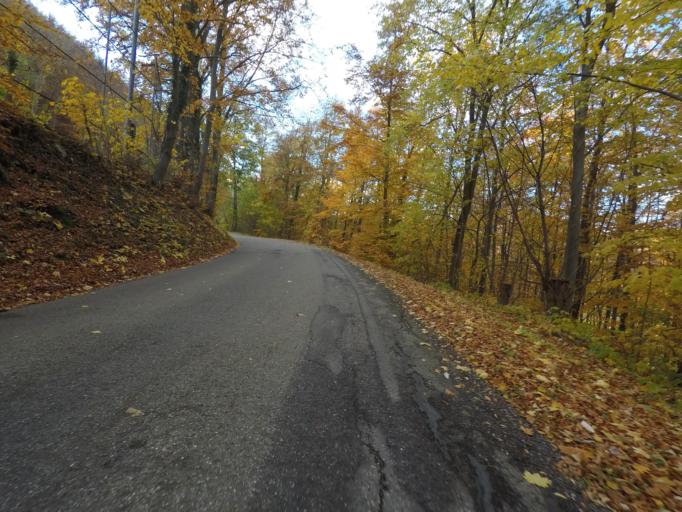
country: DE
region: Baden-Wuerttemberg
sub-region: Tuebingen Region
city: Pfullingen
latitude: 48.4239
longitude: 9.2470
